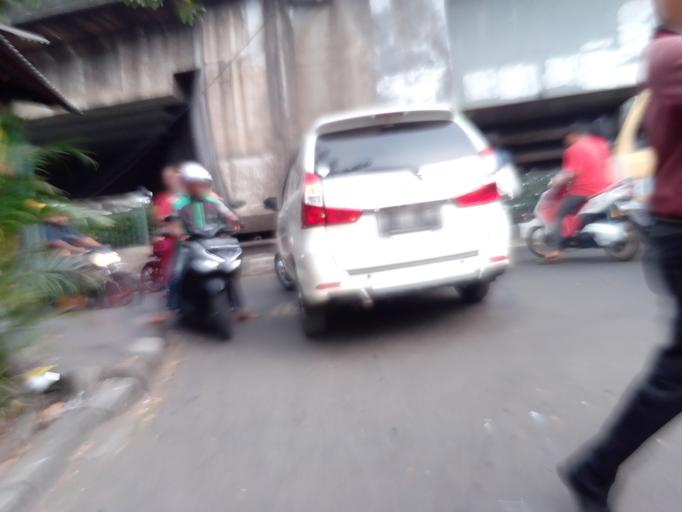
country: ID
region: Jakarta Raya
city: Jakarta
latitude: -6.1658
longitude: 106.8006
